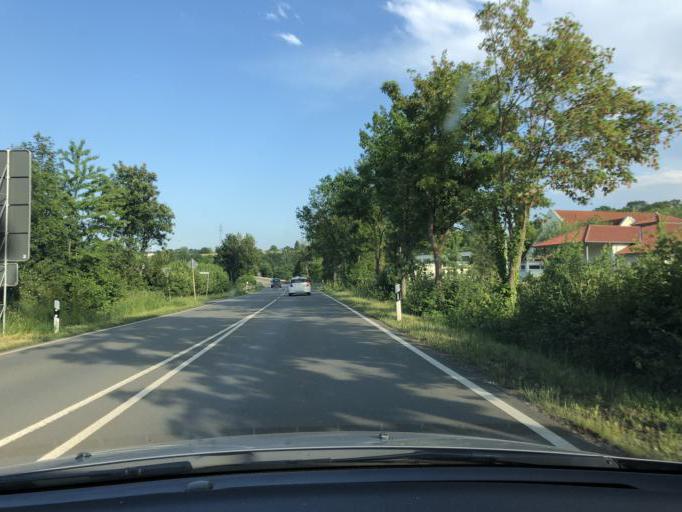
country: DE
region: Hesse
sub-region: Regierungsbezirk Kassel
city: Guxhagen
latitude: 51.2002
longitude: 9.4755
